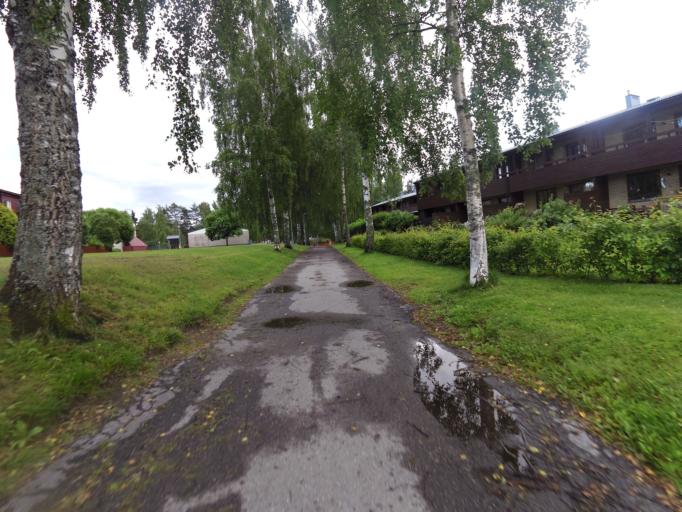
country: SE
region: Gaevleborg
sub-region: Gavle Kommun
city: Gavle
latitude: 60.6932
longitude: 17.1067
